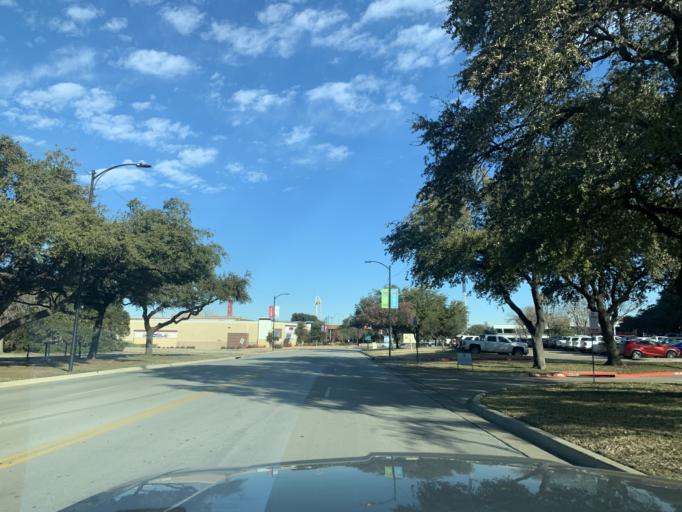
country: US
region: Texas
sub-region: Tarrant County
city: Arlington
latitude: 32.7495
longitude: -97.0687
